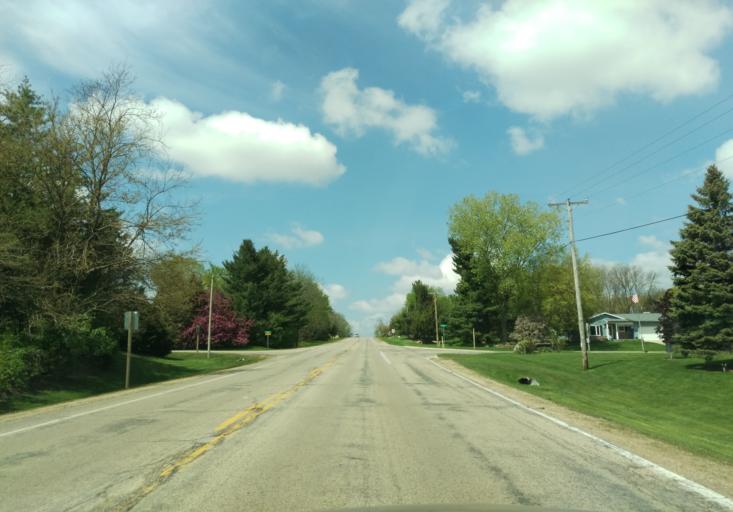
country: US
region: Wisconsin
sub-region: Dane County
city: Cross Plains
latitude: 43.0602
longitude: -89.5947
